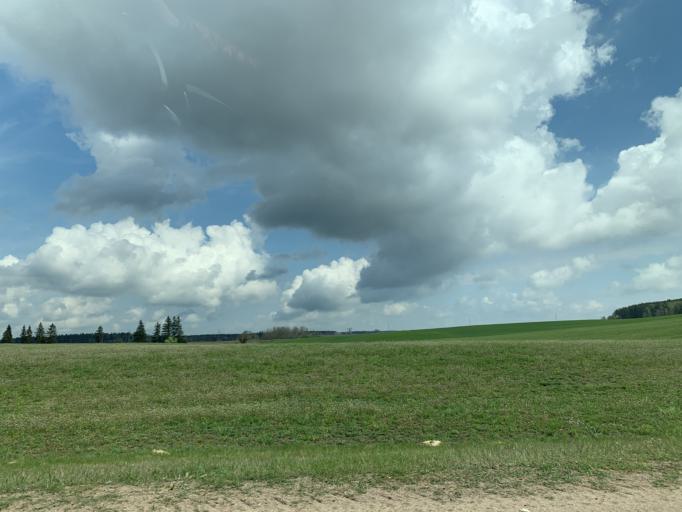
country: BY
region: Minsk
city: Nyasvizh
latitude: 53.2497
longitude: 26.6926
